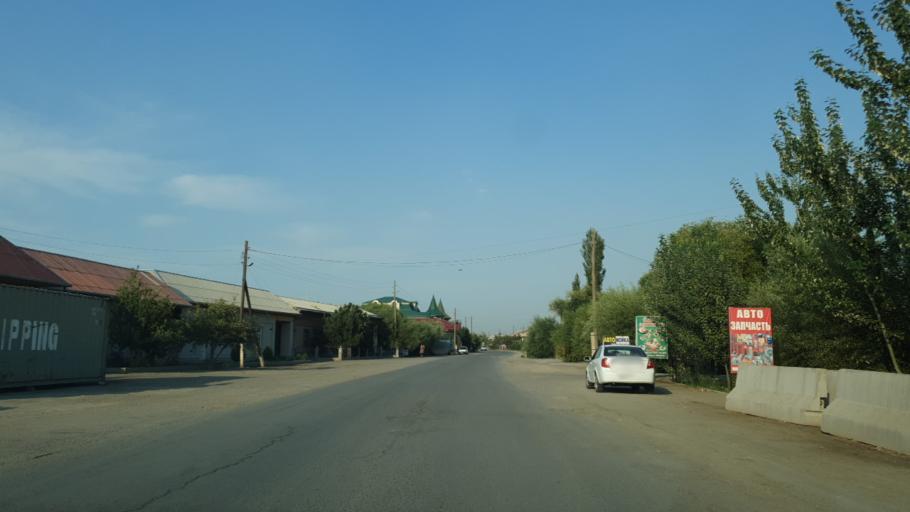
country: UZ
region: Fergana
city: Yaypan
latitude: 40.3704
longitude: 70.7708
